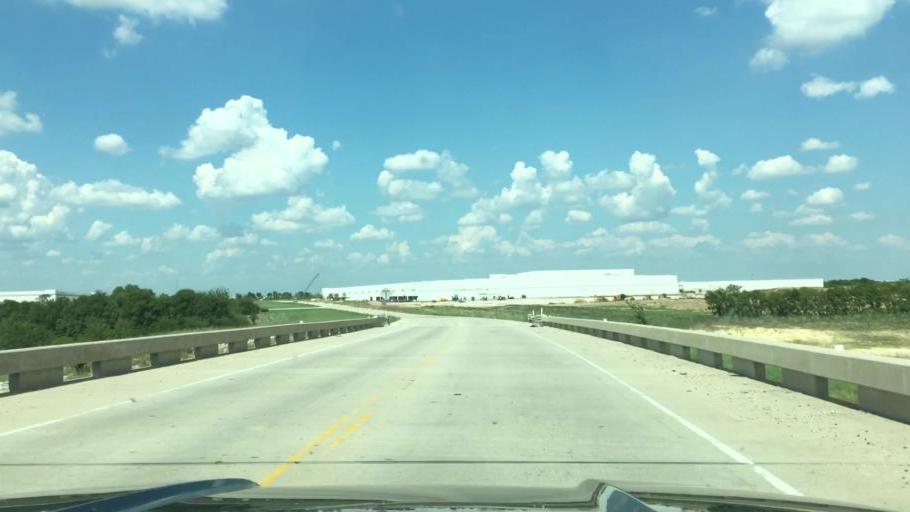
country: US
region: Texas
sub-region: Tarrant County
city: Haslet
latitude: 32.9802
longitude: -97.3424
